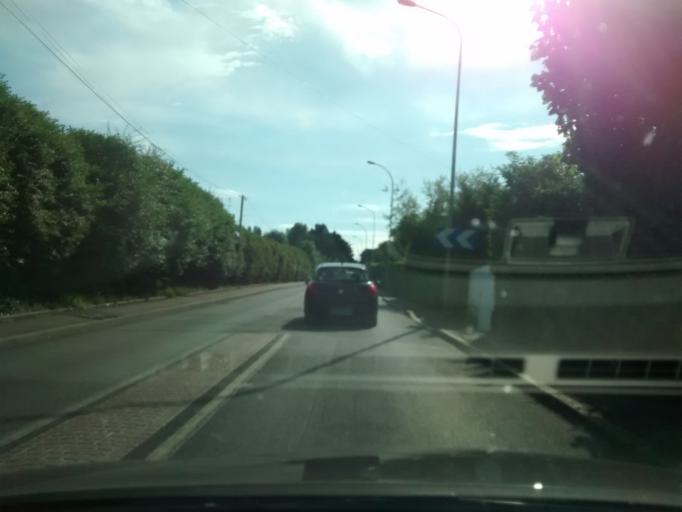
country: FR
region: Lower Normandy
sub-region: Departement du Calvados
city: Blonville-sur-Mer
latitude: 49.3465
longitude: 0.0446
